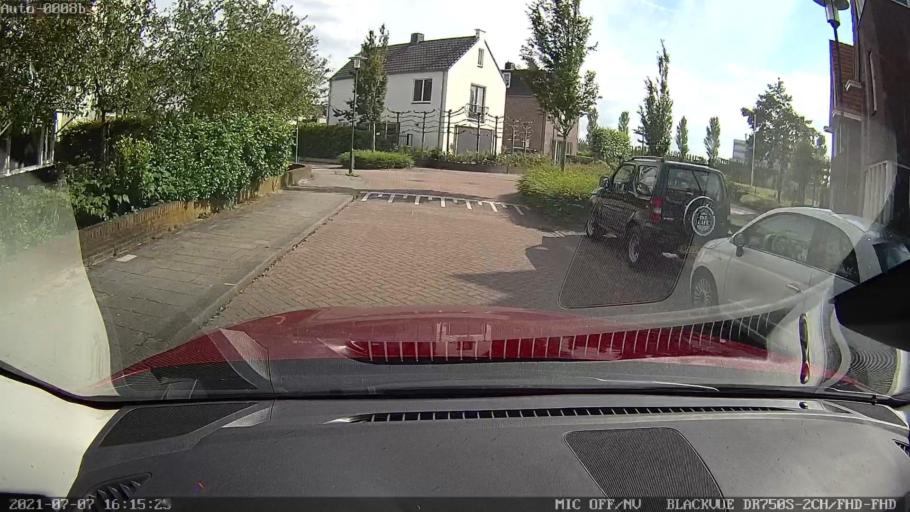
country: NL
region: Zeeland
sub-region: Gemeente Middelburg
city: Middelburg
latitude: 51.4821
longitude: 3.6372
